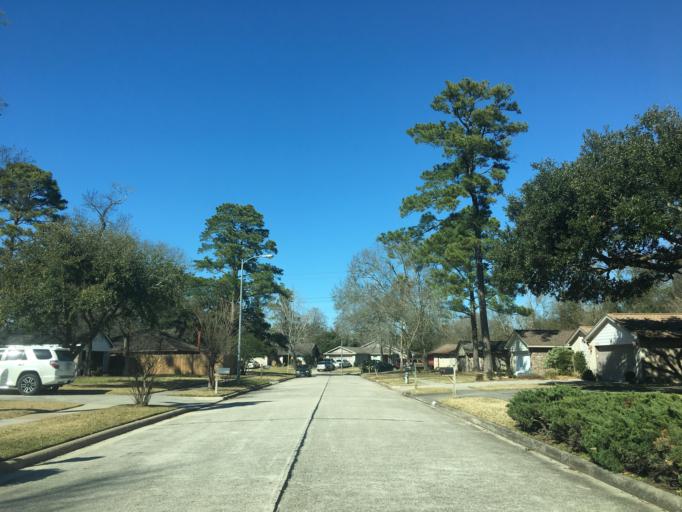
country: US
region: Texas
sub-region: Harris County
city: Spring
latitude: 30.0880
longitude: -95.4660
